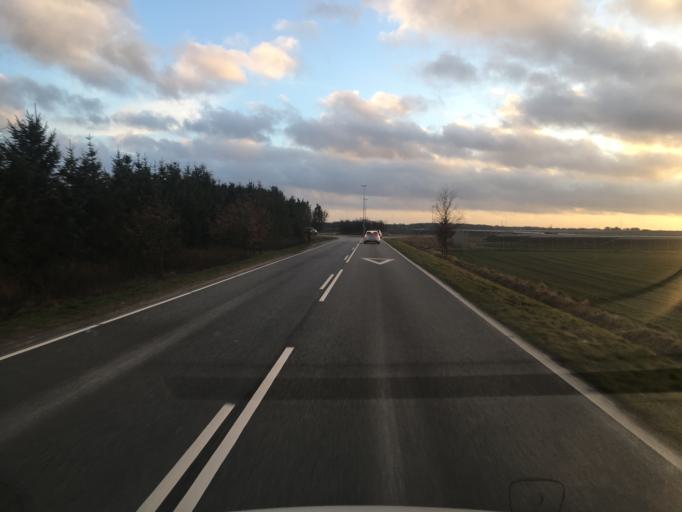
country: DK
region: South Denmark
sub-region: Aabenraa Kommune
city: Tinglev
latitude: 54.9509
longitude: 9.2773
